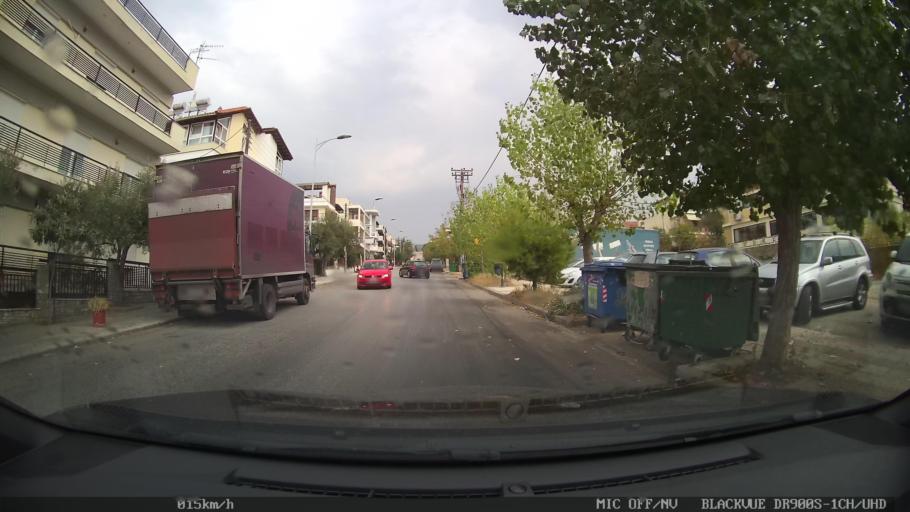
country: GR
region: Central Macedonia
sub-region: Nomos Thessalonikis
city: Pylaia
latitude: 40.6087
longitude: 22.9929
